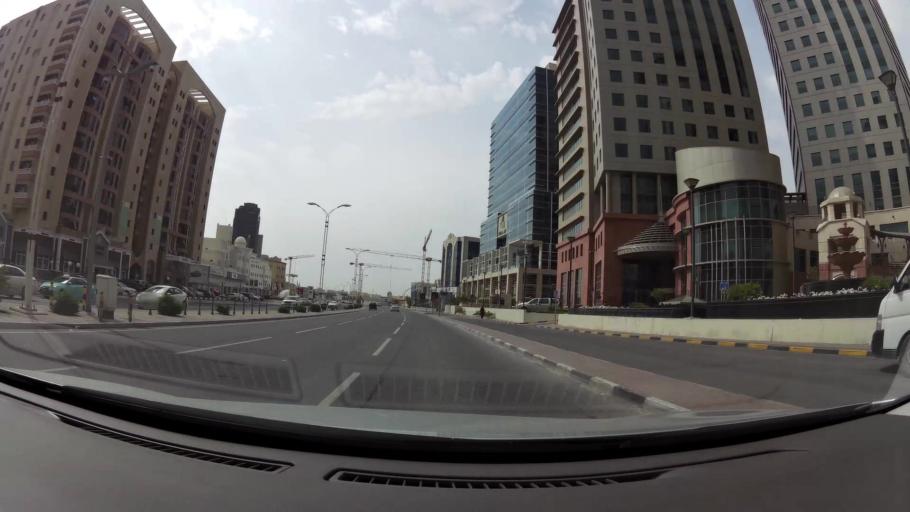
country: QA
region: Baladiyat ad Dawhah
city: Doha
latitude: 25.2859
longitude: 51.5056
